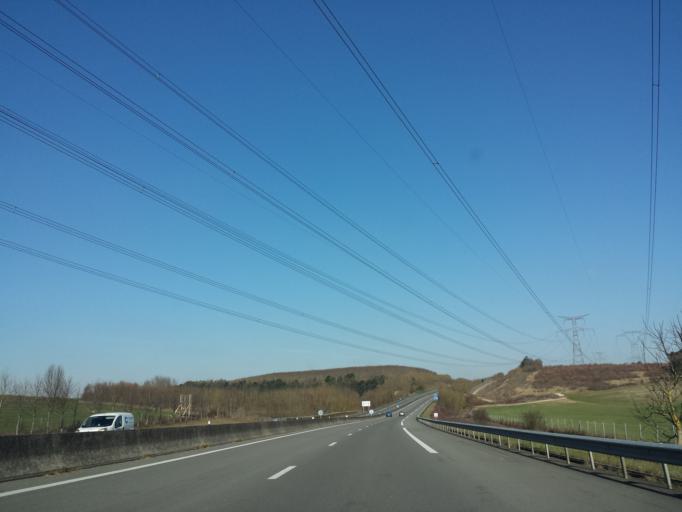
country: FR
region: Picardie
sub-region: Departement de la Somme
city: Conty
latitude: 49.7449
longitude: 2.2311
